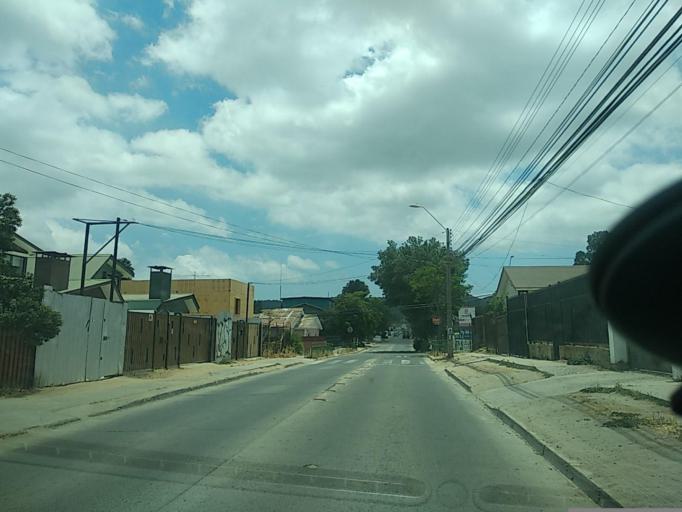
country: CL
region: Valparaiso
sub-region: Provincia de Marga Marga
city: Villa Alemana
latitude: -33.0367
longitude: -71.4056
